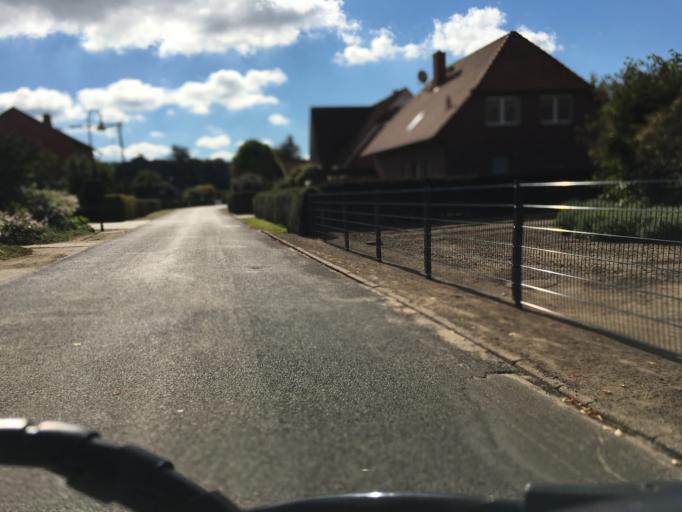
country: DE
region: Lower Saxony
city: Bardowick
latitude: 53.2963
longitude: 10.3988
